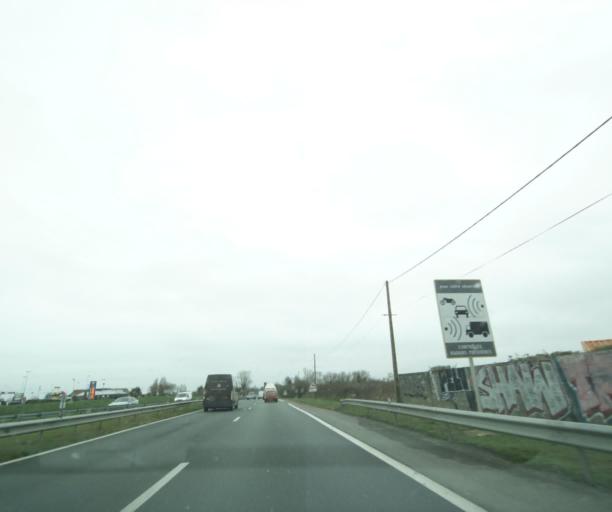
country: FR
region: Poitou-Charentes
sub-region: Departement de la Charente-Maritime
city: Angoulins
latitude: 46.1108
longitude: -1.1011
